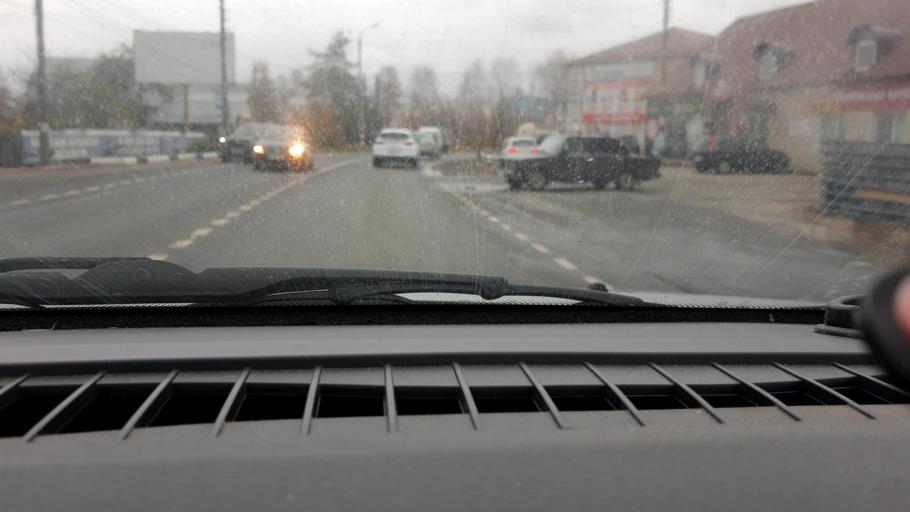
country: RU
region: Nizjnij Novgorod
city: Neklyudovo
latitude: 56.4037
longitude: 44.0065
